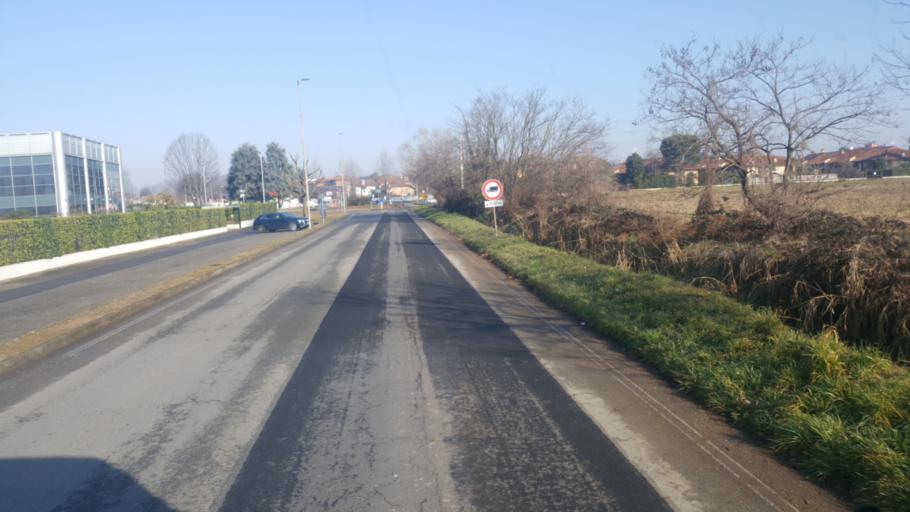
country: IT
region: Lombardy
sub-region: Citta metropolitana di Milano
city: Marcallo
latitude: 45.4775
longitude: 8.8695
